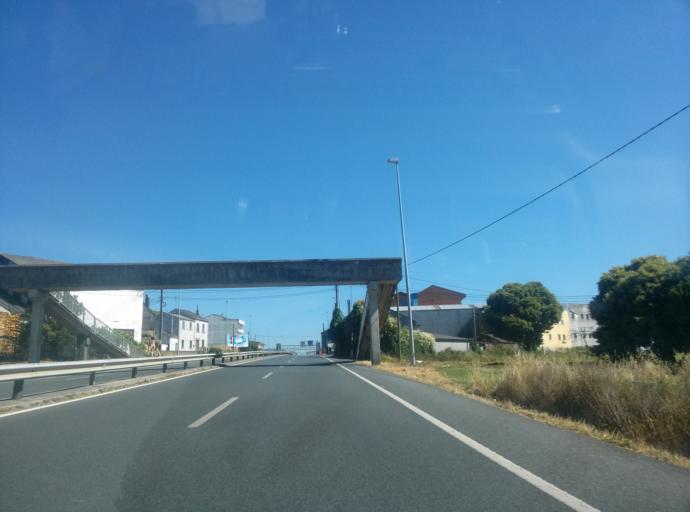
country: ES
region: Galicia
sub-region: Provincia de Lugo
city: Lugo
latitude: 43.0404
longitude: -7.5791
